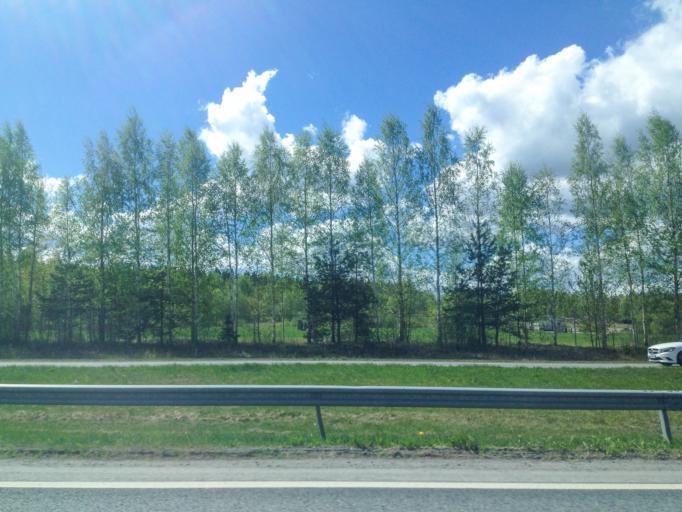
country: FI
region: Haeme
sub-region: Haemeenlinna
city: Parola
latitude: 61.0239
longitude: 24.4036
